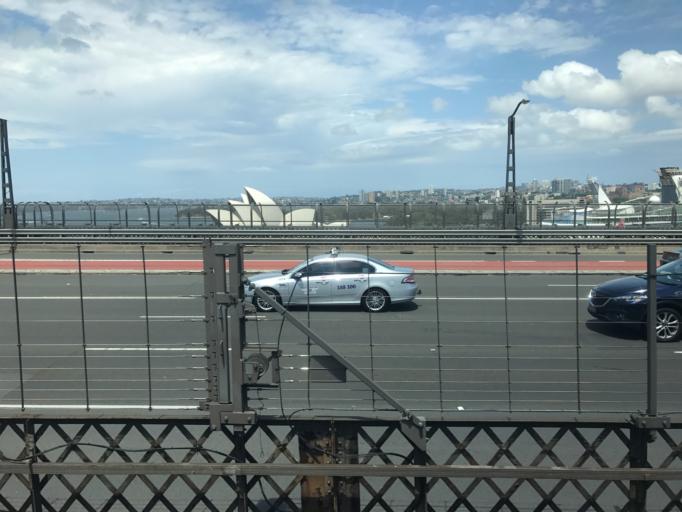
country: AU
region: New South Wales
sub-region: North Sydney
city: Milsons Point
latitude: -33.8552
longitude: 151.2088
